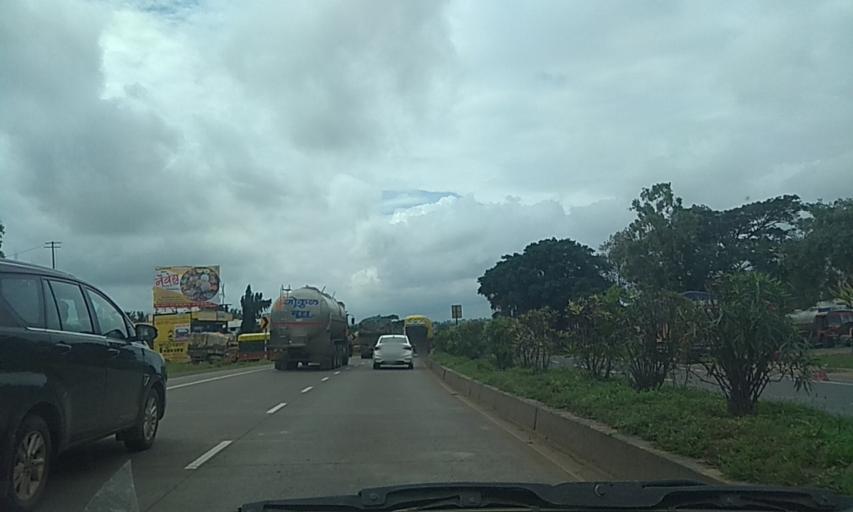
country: IN
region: Maharashtra
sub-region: Kolhapur
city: Kagal
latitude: 16.6387
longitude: 74.2785
